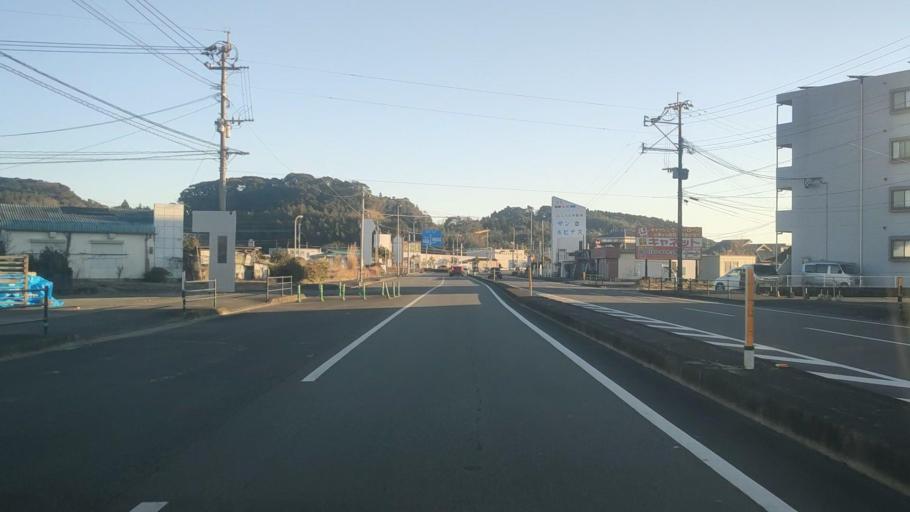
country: JP
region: Miyazaki
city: Takanabe
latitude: 32.0732
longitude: 131.4941
